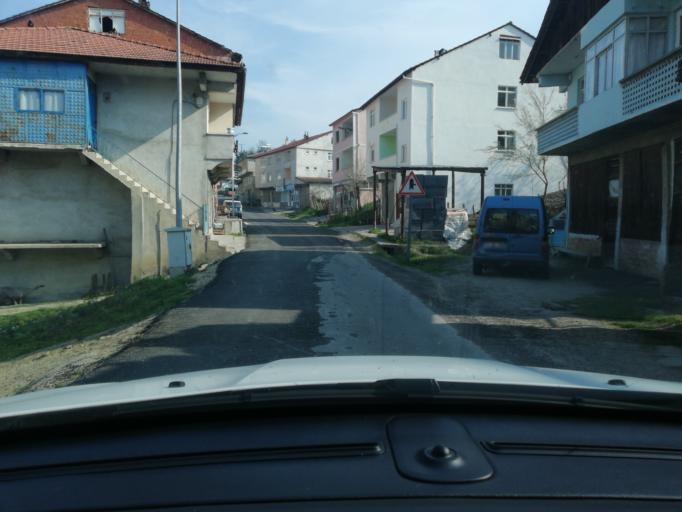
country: TR
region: Karabuk
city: Yenice
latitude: 41.2617
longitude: 32.3636
